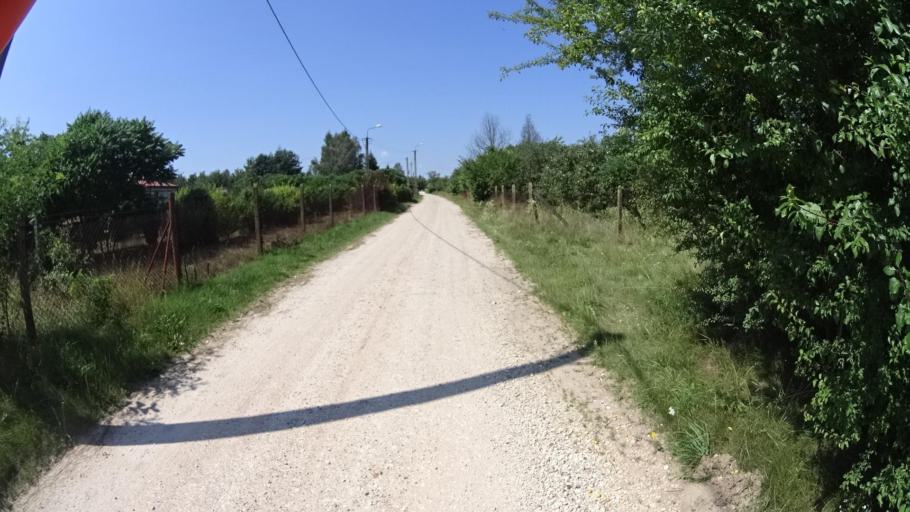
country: PL
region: Masovian Voivodeship
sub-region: Powiat piaseczynski
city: Tarczyn
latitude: 51.9763
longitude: 20.8578
